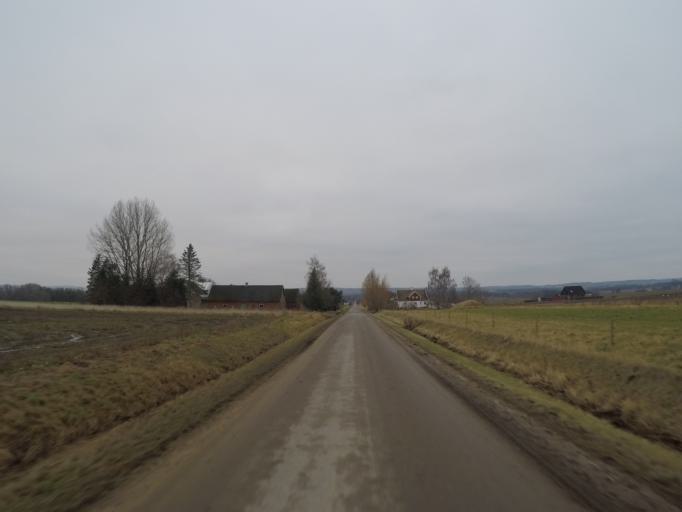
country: SE
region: Skane
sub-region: Hoors Kommun
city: Loberod
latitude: 55.7556
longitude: 13.4237
